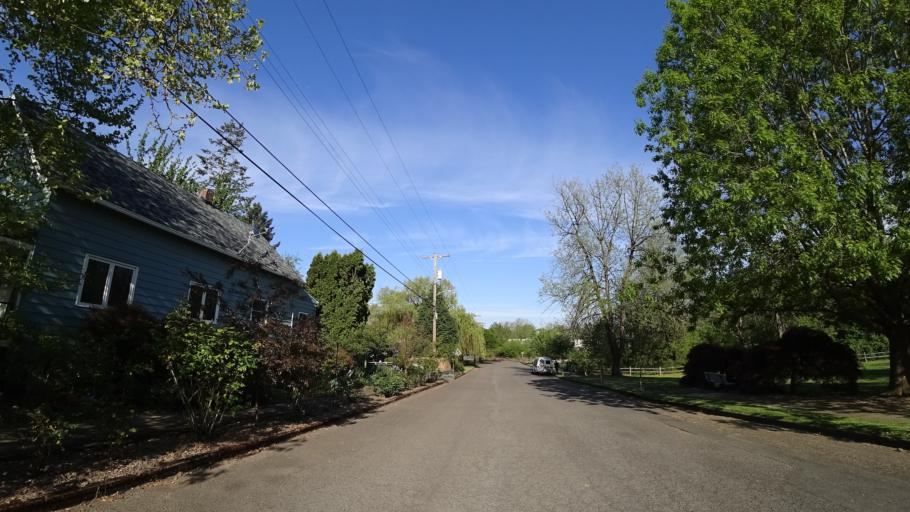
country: US
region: Oregon
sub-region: Clackamas County
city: Milwaukie
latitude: 45.4614
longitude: -122.6429
